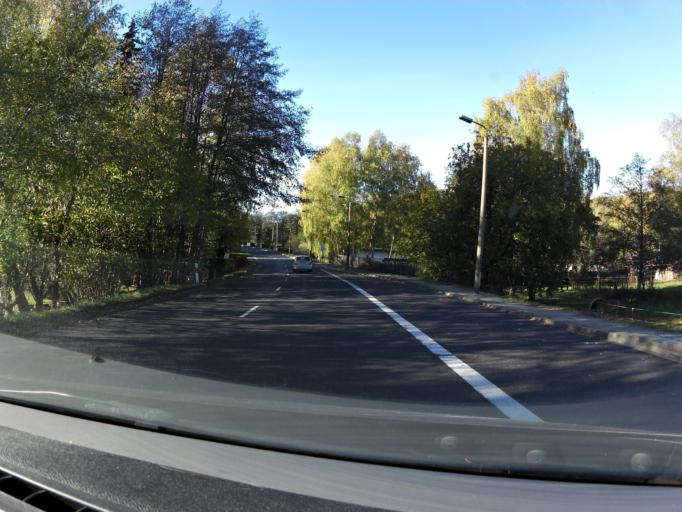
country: DE
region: Thuringia
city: Martinroda
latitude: 50.6981
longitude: 10.8926
